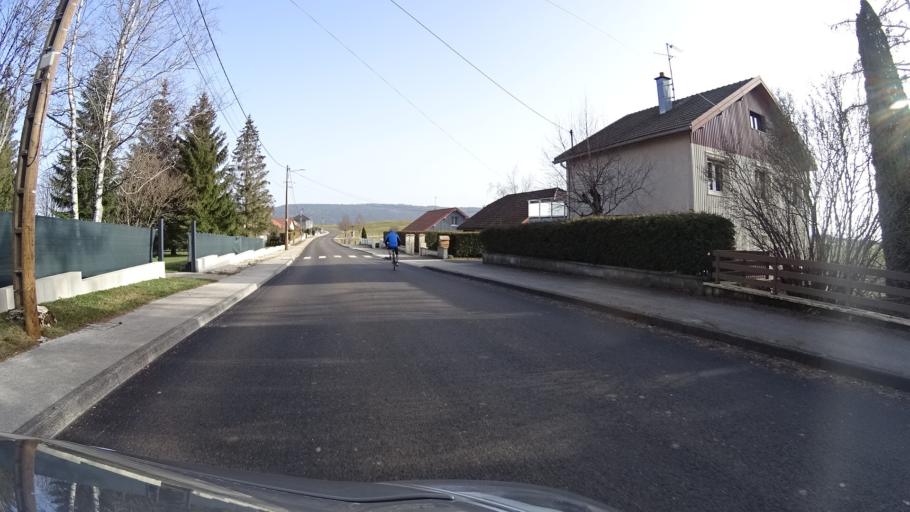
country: FR
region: Franche-Comte
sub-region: Departement du Doubs
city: Frasne
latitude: 46.8710
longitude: 6.1880
